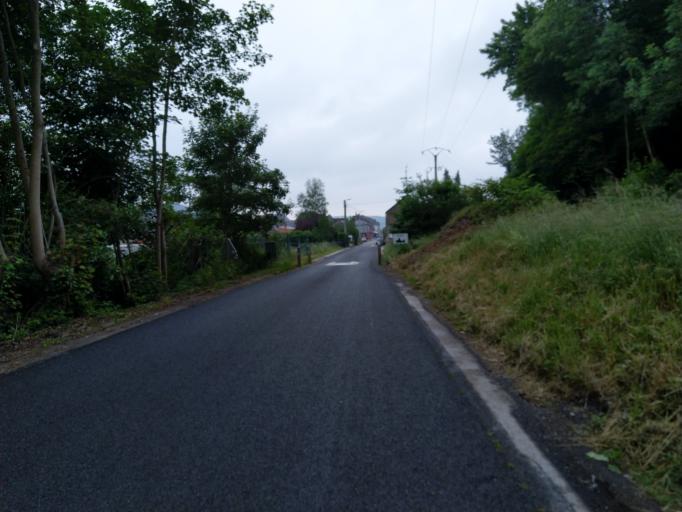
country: BE
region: Wallonia
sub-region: Province de Namur
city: Anhee
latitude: 50.3143
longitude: 4.8737
